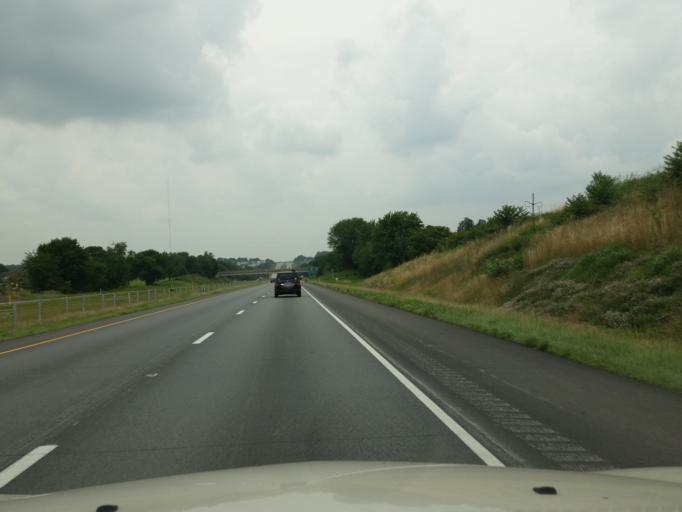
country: US
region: Pennsylvania
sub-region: Lancaster County
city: Elizabethtown
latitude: 40.1599
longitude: -76.5771
